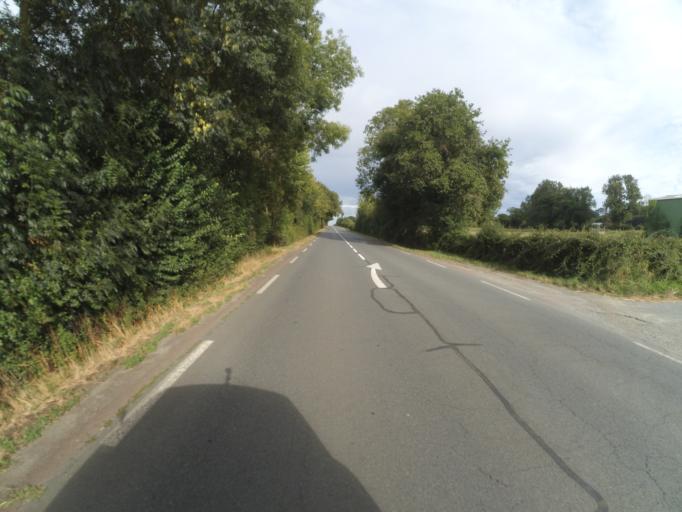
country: FR
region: Poitou-Charentes
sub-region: Departement des Deux-Sevres
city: Saint-Amand-sur-Sevre
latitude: 46.9277
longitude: -0.7716
